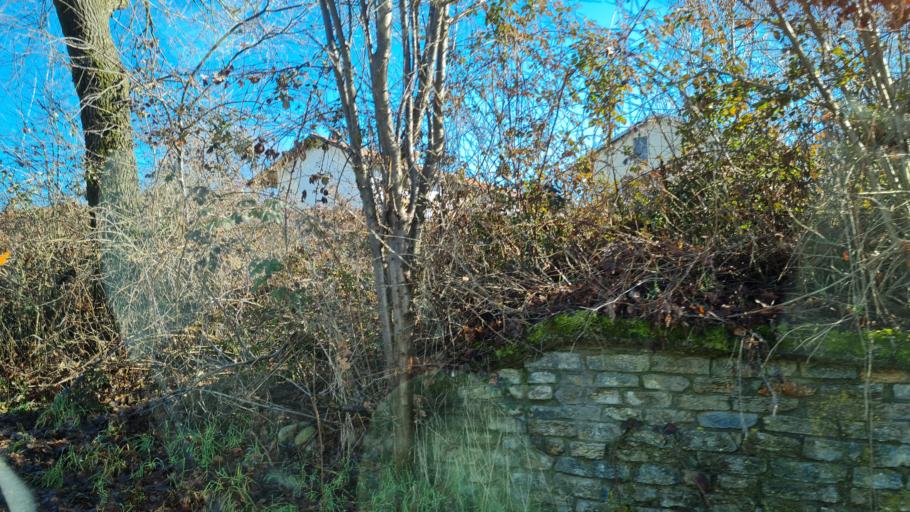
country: IT
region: Piedmont
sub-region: Provincia di Biella
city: Zubiena
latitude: 45.5034
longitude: 8.0000
